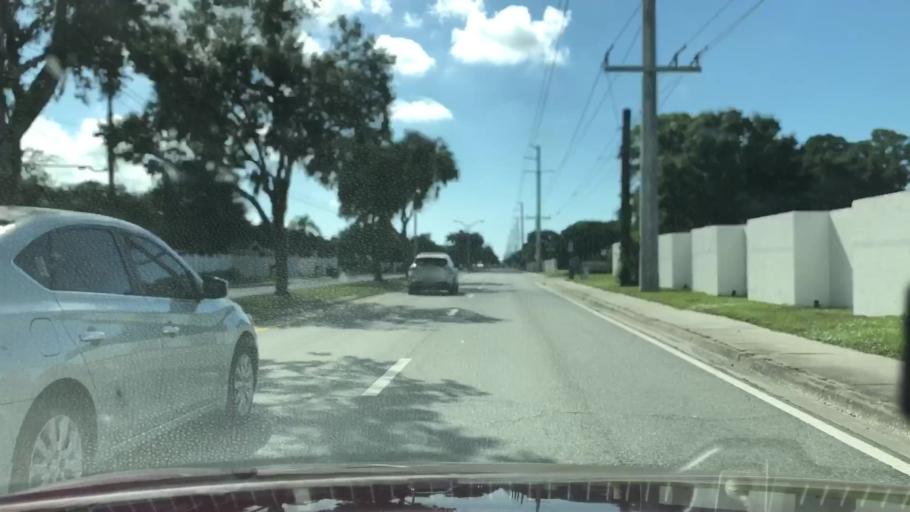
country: US
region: Florida
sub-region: Sarasota County
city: South Gate Ridge
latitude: 27.2665
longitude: -82.4977
